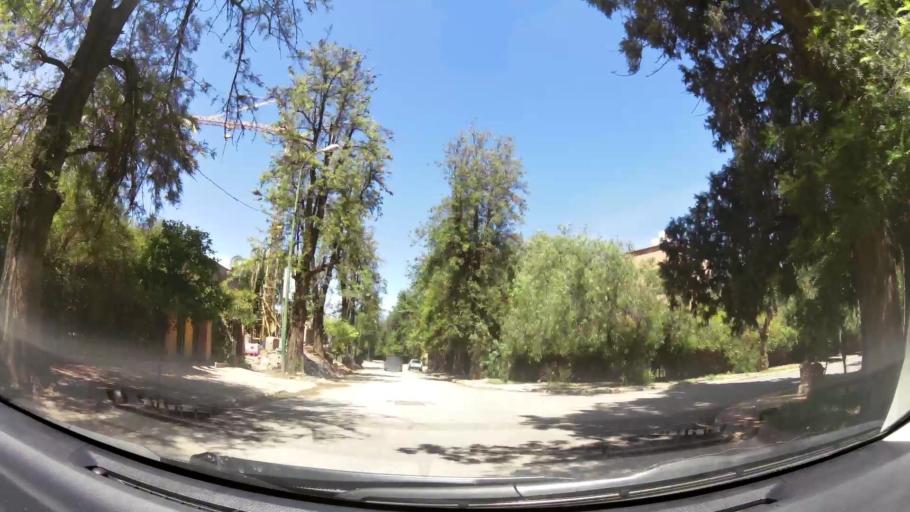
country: MA
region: Marrakech-Tensift-Al Haouz
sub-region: Marrakech
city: Marrakesh
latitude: 31.6219
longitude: -8.0090
